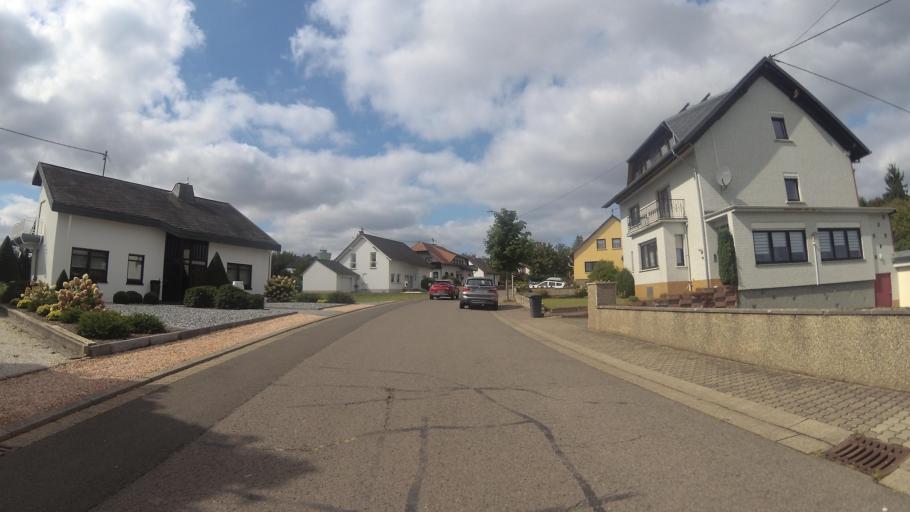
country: FR
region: Lorraine
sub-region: Departement de la Moselle
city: Carling
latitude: 49.1886
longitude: 6.7330
